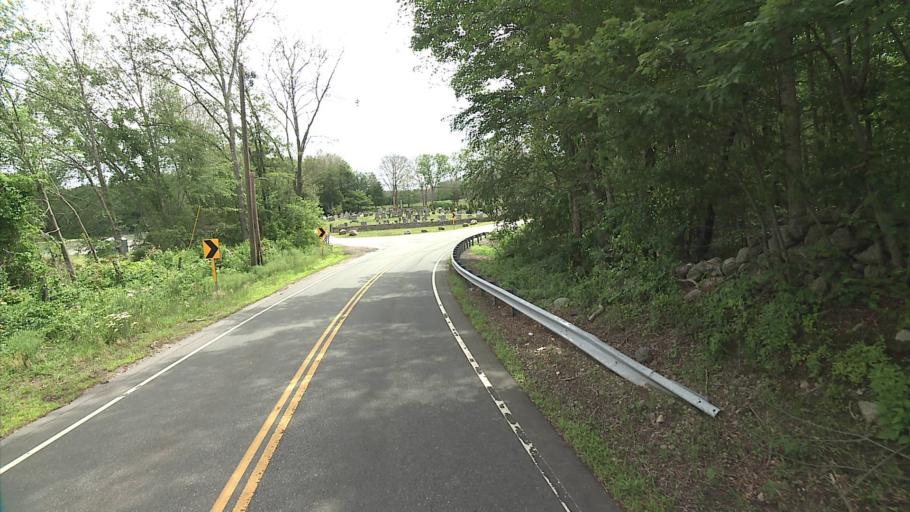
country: US
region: Connecticut
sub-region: New London County
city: Gales Ferry
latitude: 41.4515
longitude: -72.0512
